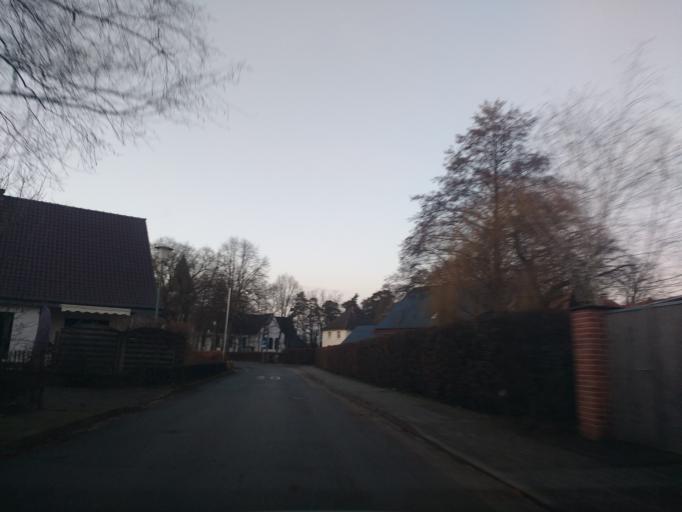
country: DE
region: North Rhine-Westphalia
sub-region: Regierungsbezirk Detmold
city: Hovelhof
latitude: 51.8479
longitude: 8.6274
